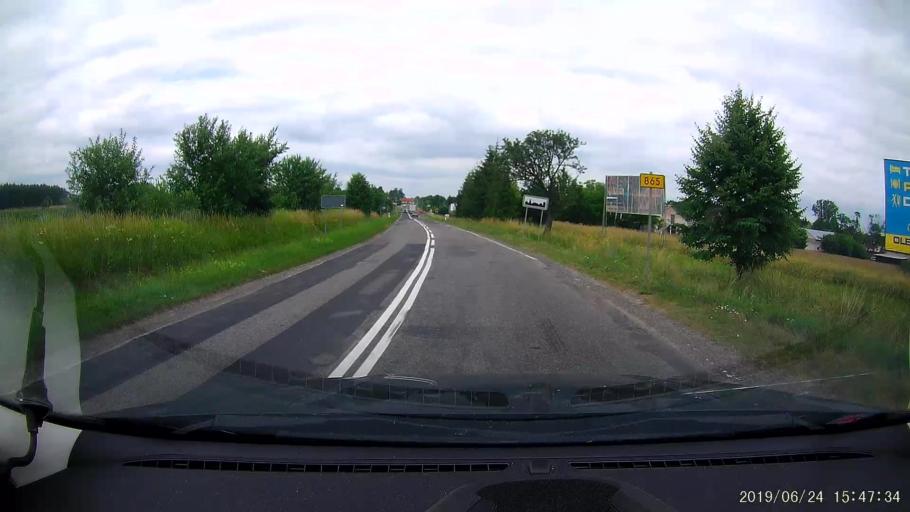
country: PL
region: Subcarpathian Voivodeship
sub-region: Powiat lubaczowski
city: Oleszyce
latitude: 50.1644
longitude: 23.0226
